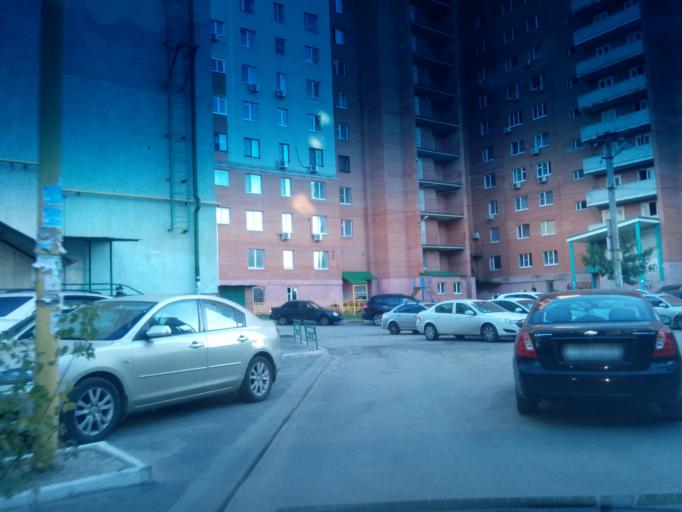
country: RU
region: Rostov
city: Severnyy
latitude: 47.2741
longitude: 39.7143
